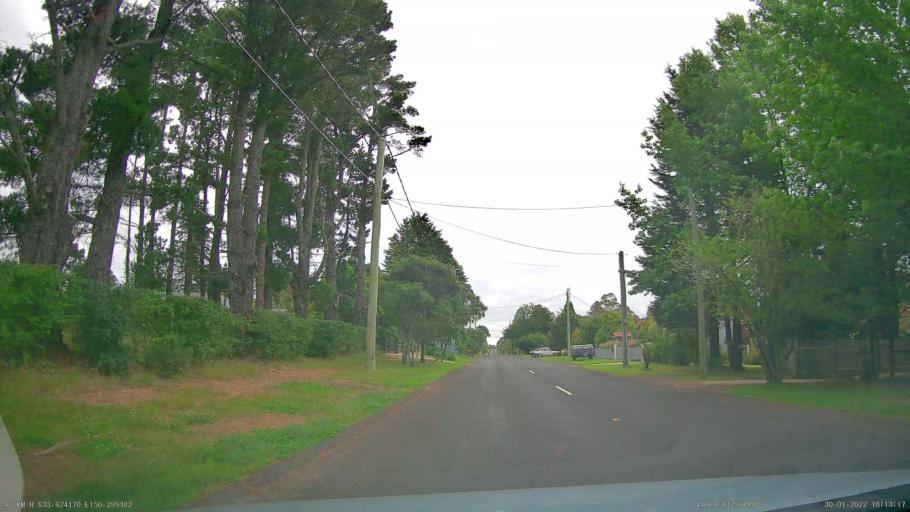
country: AU
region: New South Wales
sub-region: Blue Mountains Municipality
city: Blackheath
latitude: -33.6242
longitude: 150.2993
